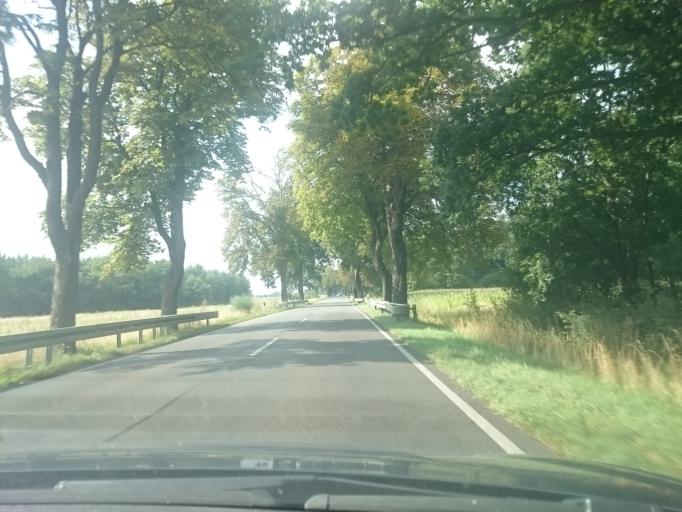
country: DE
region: Mecklenburg-Vorpommern
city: Ducherow
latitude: 53.7330
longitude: 13.8006
